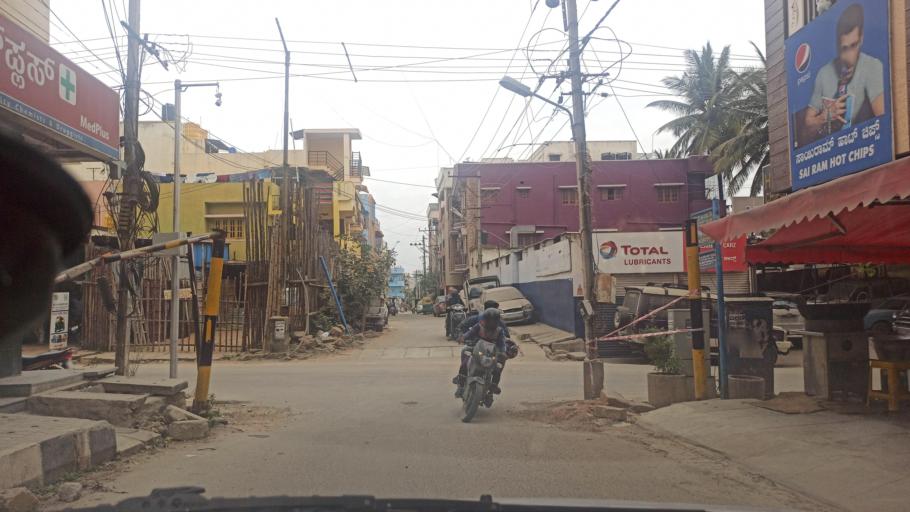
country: IN
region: Karnataka
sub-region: Bangalore Urban
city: Yelahanka
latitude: 13.0384
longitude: 77.6075
